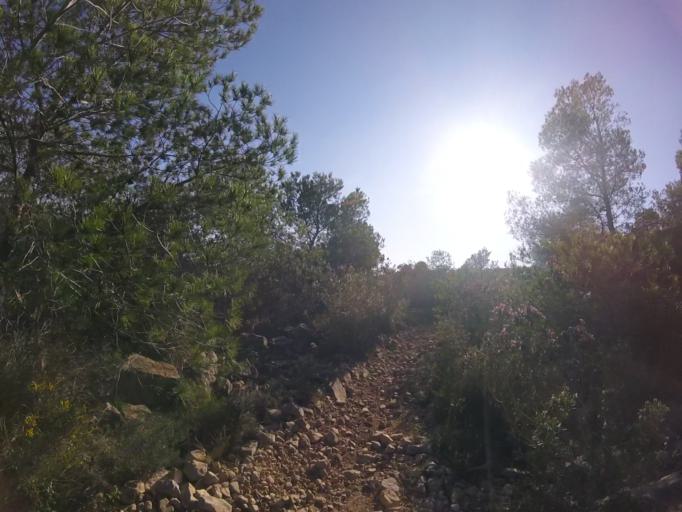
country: ES
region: Valencia
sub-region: Provincia de Castello
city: Santa Magdalena de Pulpis
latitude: 40.2985
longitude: 0.3315
